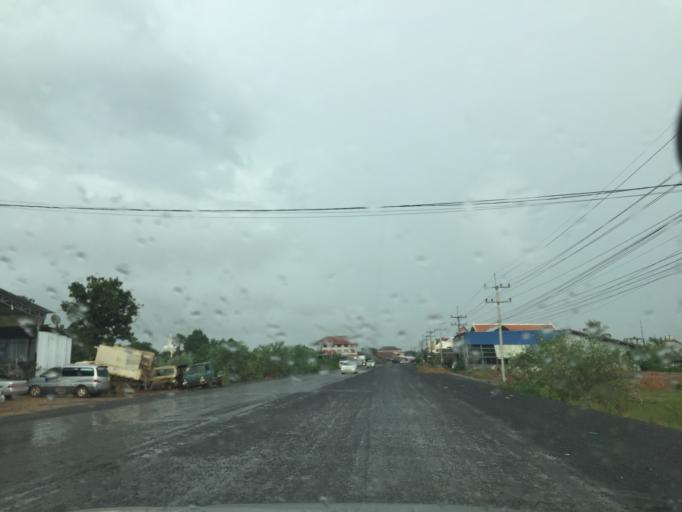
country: LA
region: Attapu
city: Attapu
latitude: 14.8239
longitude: 106.8099
